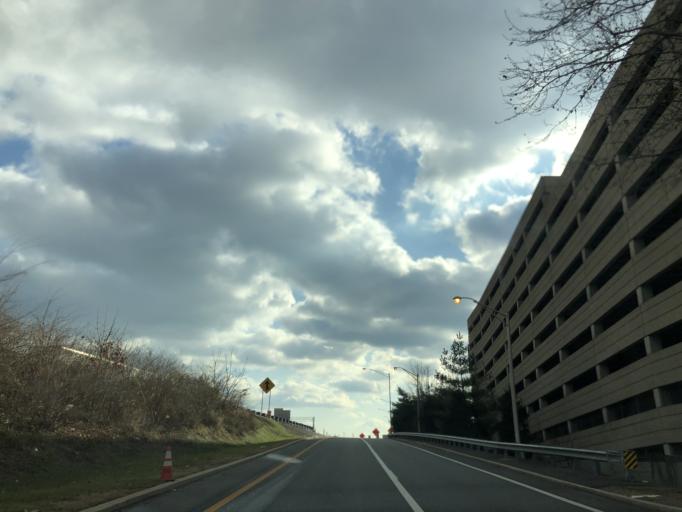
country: US
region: New Jersey
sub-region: Camden County
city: Camden
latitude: 39.9421
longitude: -75.1138
